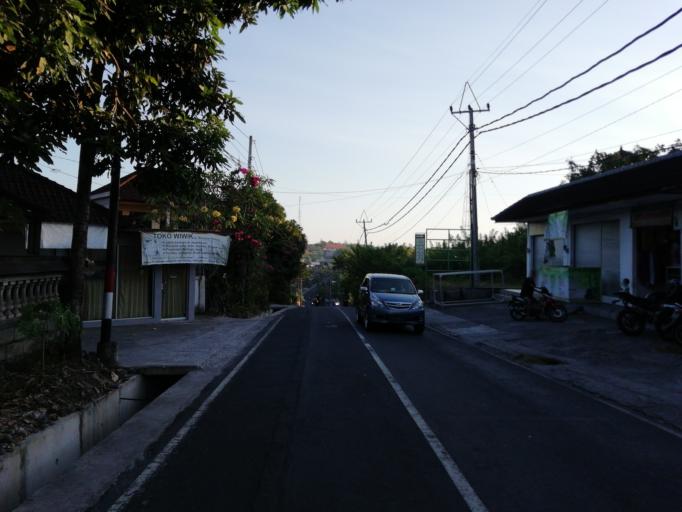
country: ID
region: Bali
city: Bualu
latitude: -8.8202
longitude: 115.1891
